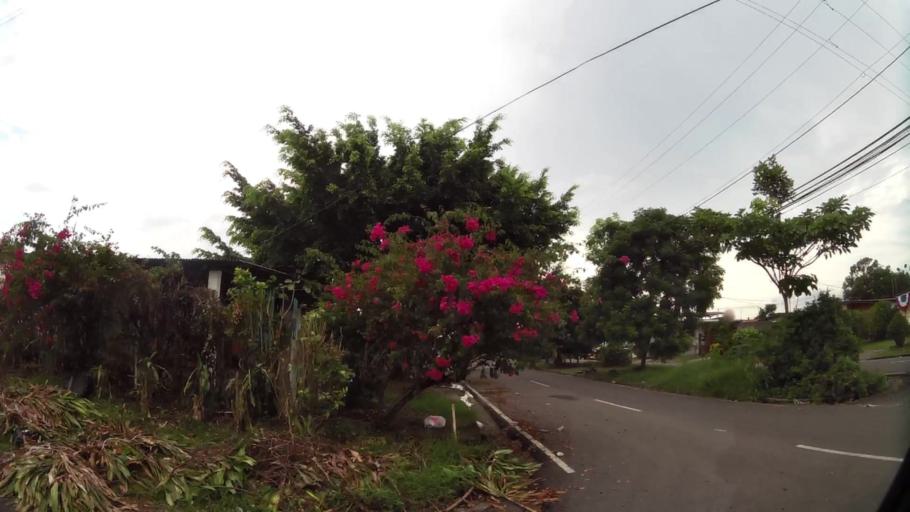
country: PA
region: Panama
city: Cabra Numero Uno
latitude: 9.0914
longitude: -79.3426
